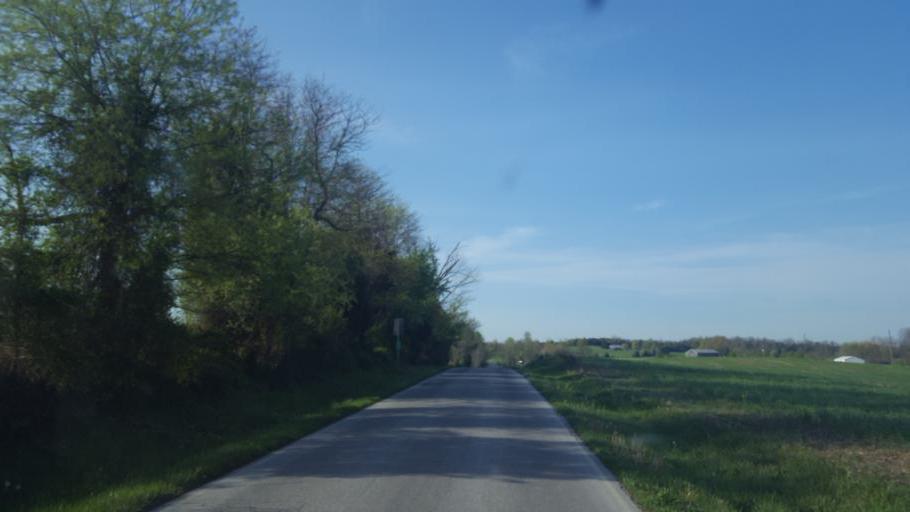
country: US
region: Kentucky
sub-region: Hardin County
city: Elizabethtown
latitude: 37.4947
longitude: -85.9612
